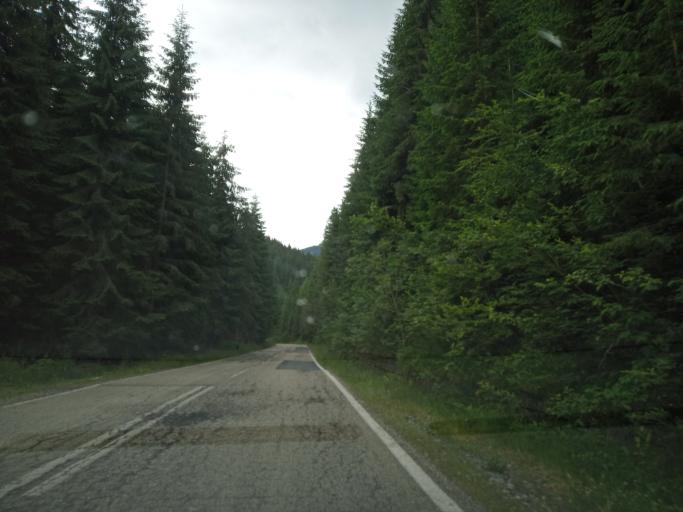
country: RO
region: Valcea
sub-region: Comuna Voineasa
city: Voineasa
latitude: 45.4227
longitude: 23.7520
